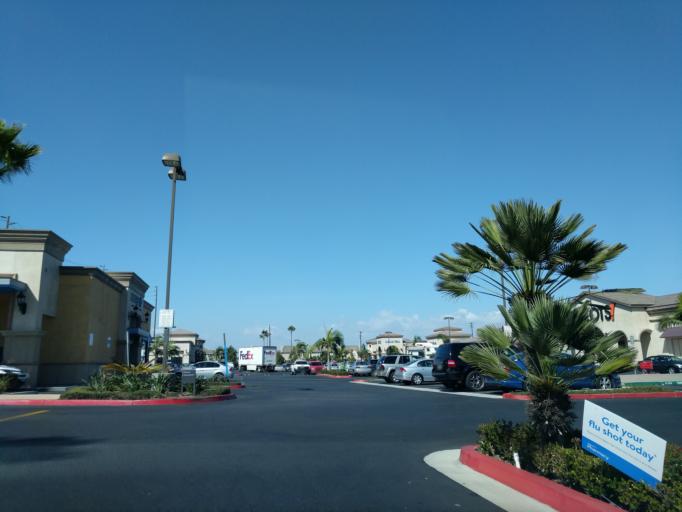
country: US
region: California
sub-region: Orange County
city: Huntington Beach
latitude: 33.6557
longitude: -117.9877
